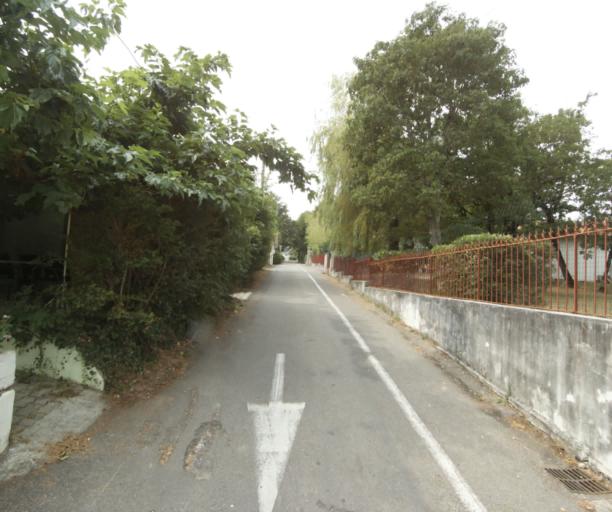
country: FR
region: Midi-Pyrenees
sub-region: Departement de la Haute-Garonne
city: Revel
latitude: 43.4394
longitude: 2.0212
